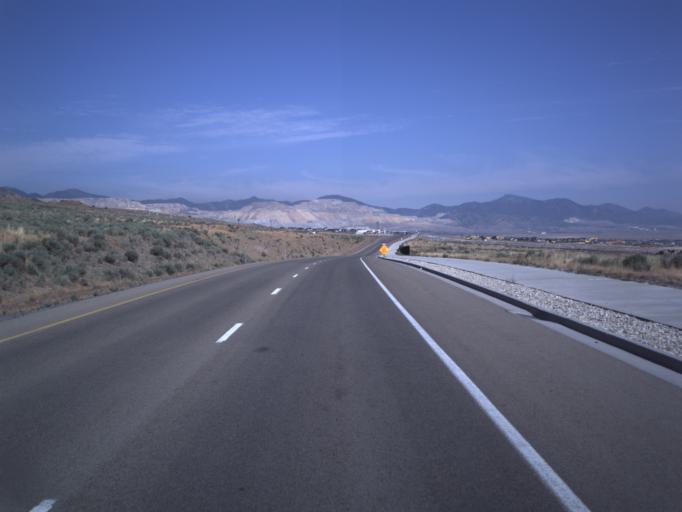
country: US
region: Utah
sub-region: Salt Lake County
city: Bluffdale
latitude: 40.4723
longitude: -111.9706
